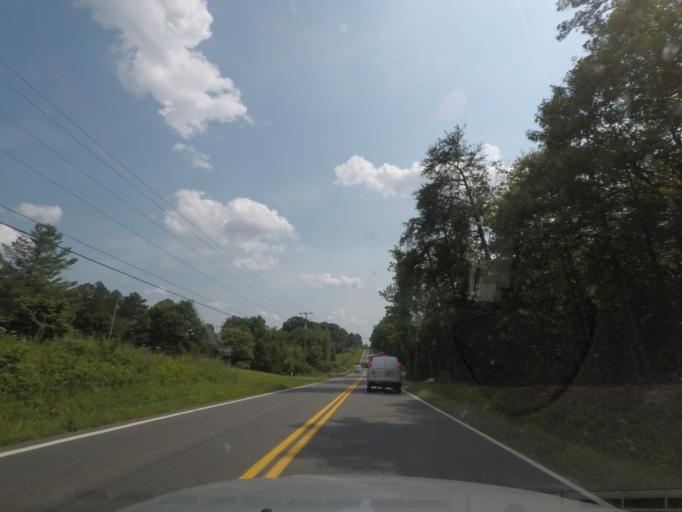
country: US
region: Virginia
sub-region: Fluvanna County
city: Palmyra
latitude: 37.9251
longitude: -78.2509
